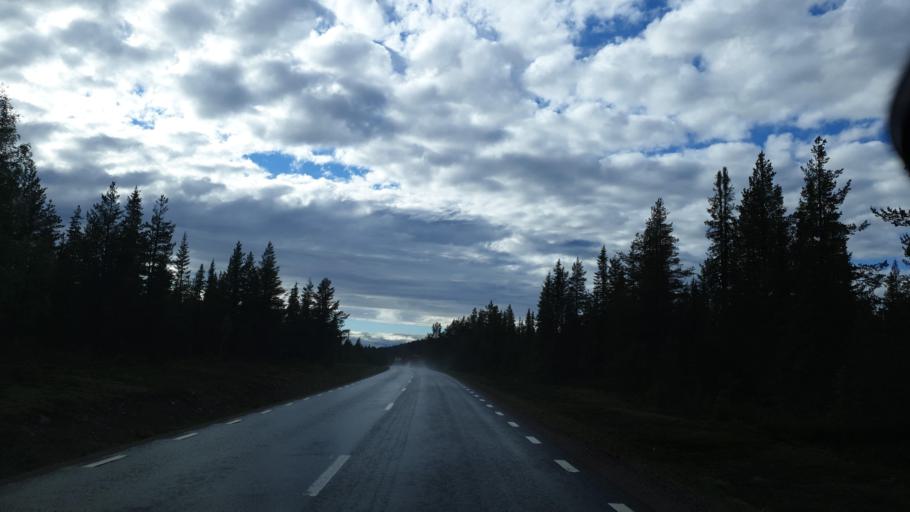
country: SE
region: Norrbotten
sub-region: Arjeplogs Kommun
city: Arjeplog
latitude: 65.9143
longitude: 18.3322
